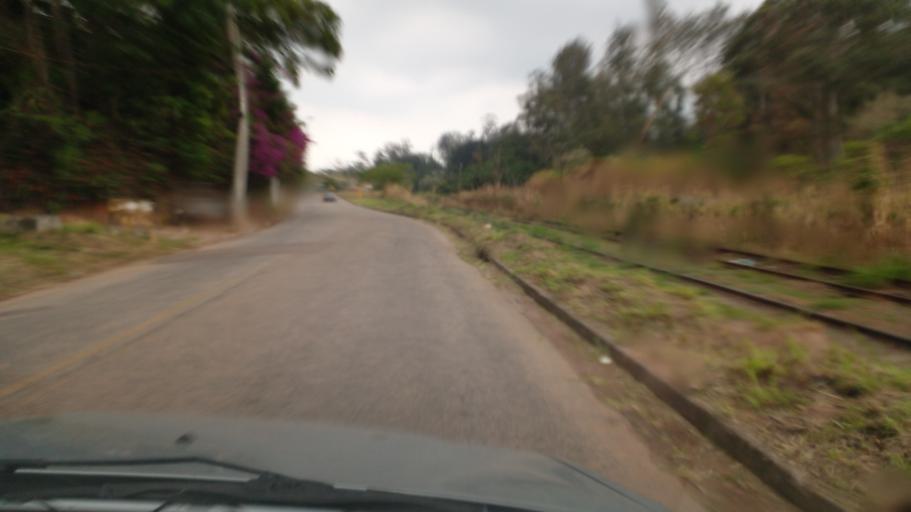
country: BR
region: Sao Paulo
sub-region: Jundiai
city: Jundiai
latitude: -23.1417
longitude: -46.9076
